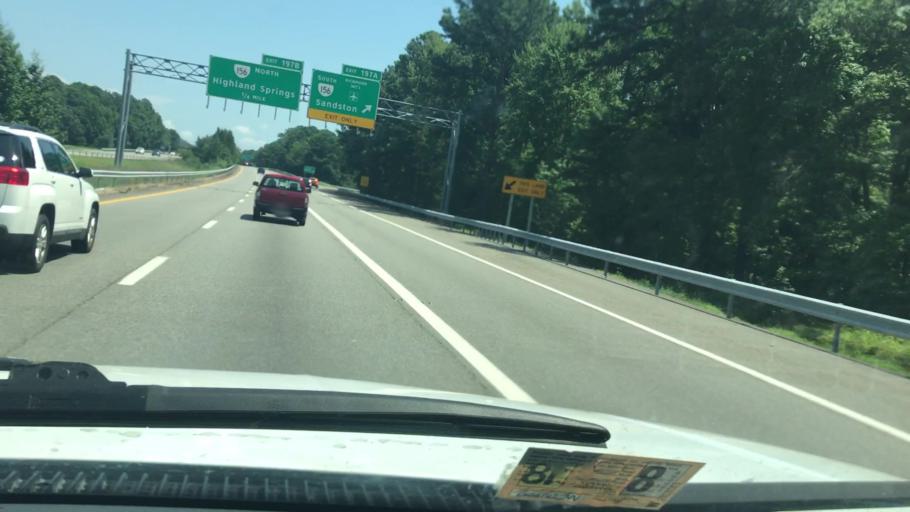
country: US
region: Virginia
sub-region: Henrico County
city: Highland Springs
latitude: 37.5300
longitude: -77.3331
